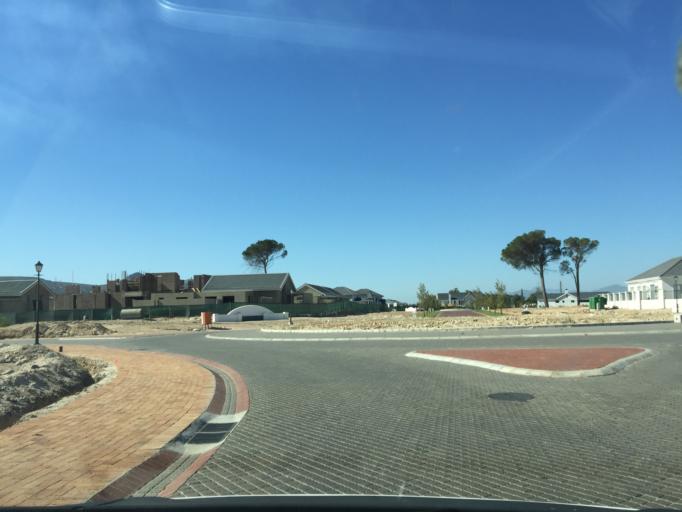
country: ZA
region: Western Cape
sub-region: Cape Winelands District Municipality
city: Paarl
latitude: -33.8085
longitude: 18.9622
